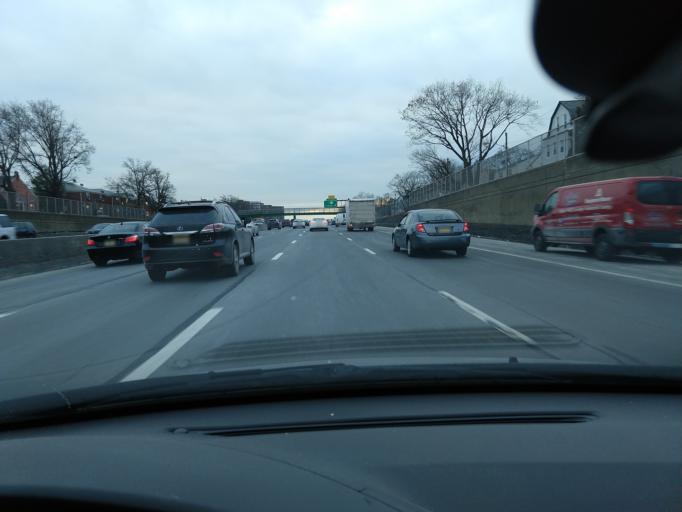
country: US
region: New Jersey
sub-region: Essex County
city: Irvington
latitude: 40.7356
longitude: -74.2193
